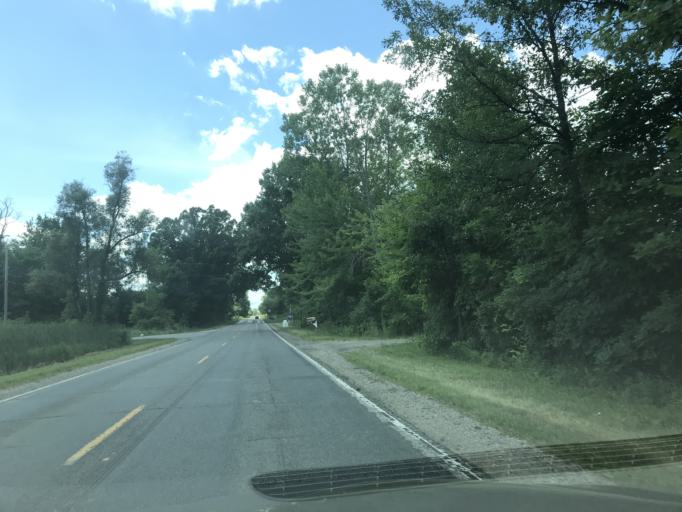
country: US
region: Michigan
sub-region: Ingham County
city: Leslie
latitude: 42.4511
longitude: -84.4963
